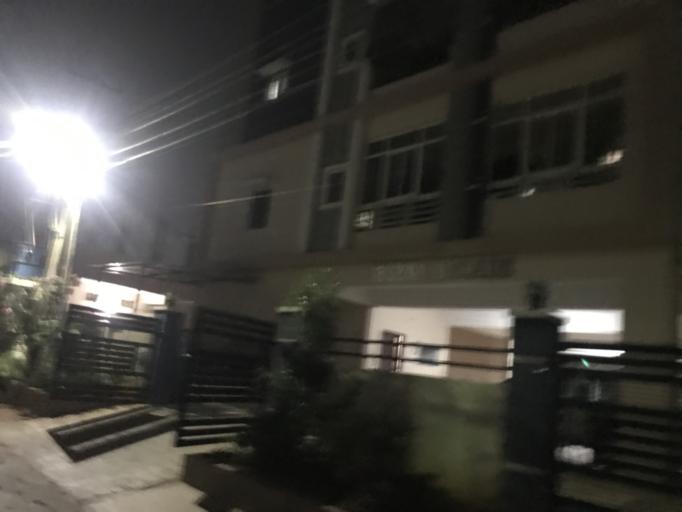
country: IN
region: Telangana
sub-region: Rangareddi
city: Secunderabad
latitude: 17.4893
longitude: 78.6022
